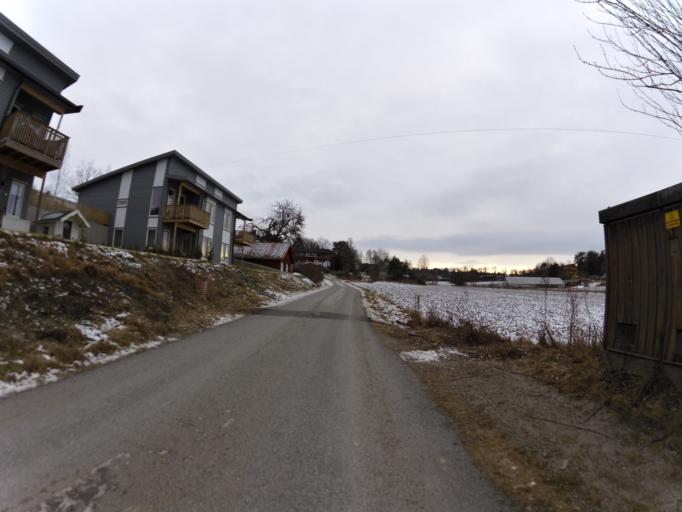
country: NO
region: Ostfold
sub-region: Fredrikstad
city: Fredrikstad
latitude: 59.2034
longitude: 10.8840
